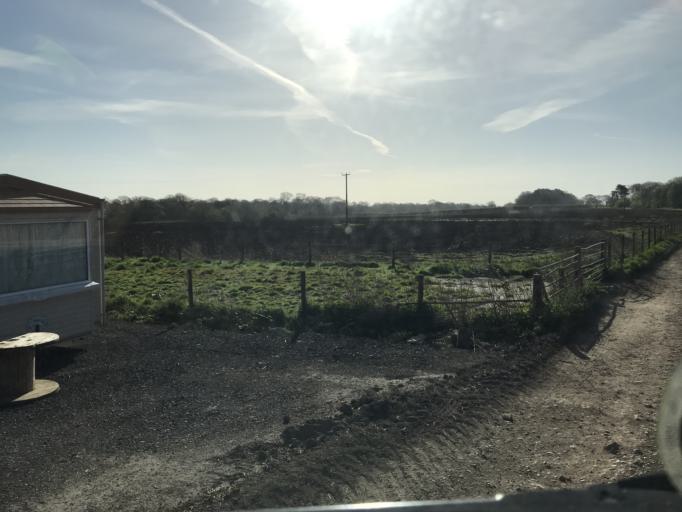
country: GB
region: England
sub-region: Cheshire East
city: Middlewich
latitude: 53.2258
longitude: -2.4771
